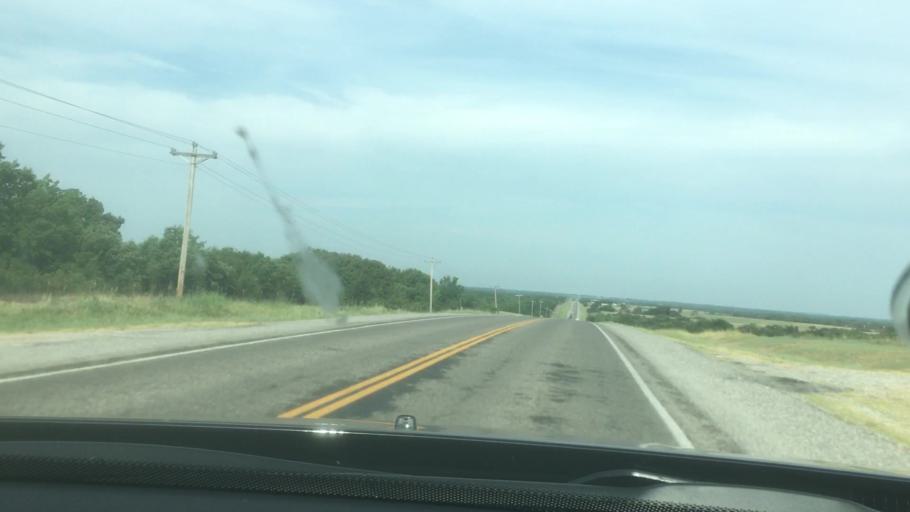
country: US
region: Oklahoma
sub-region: Garvin County
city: Stratford
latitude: 34.7966
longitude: -97.0694
